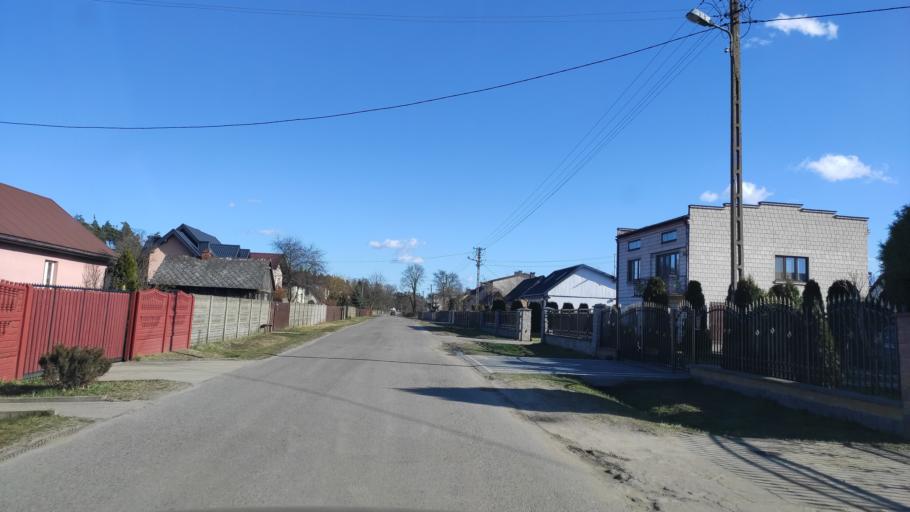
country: PL
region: Masovian Voivodeship
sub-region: Powiat radomski
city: Jastrzebia
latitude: 51.4582
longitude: 21.2636
